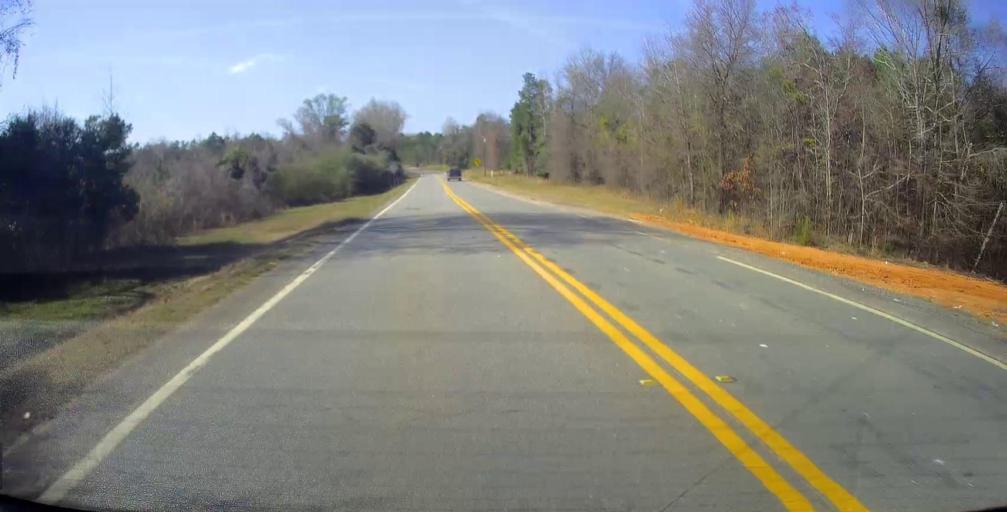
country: US
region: Georgia
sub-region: Wilkinson County
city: Gordon
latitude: 32.8523
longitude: -83.3441
